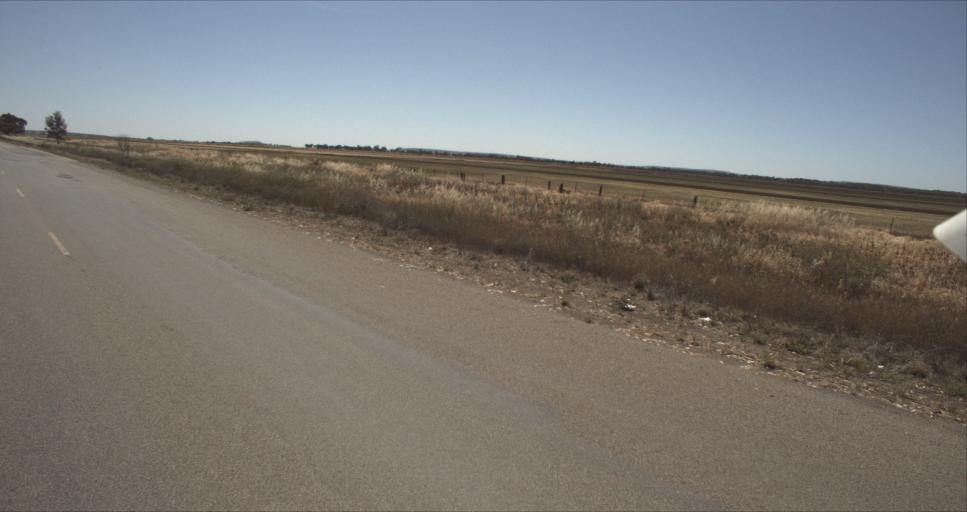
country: AU
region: New South Wales
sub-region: Leeton
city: Leeton
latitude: -34.4982
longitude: 146.2874
